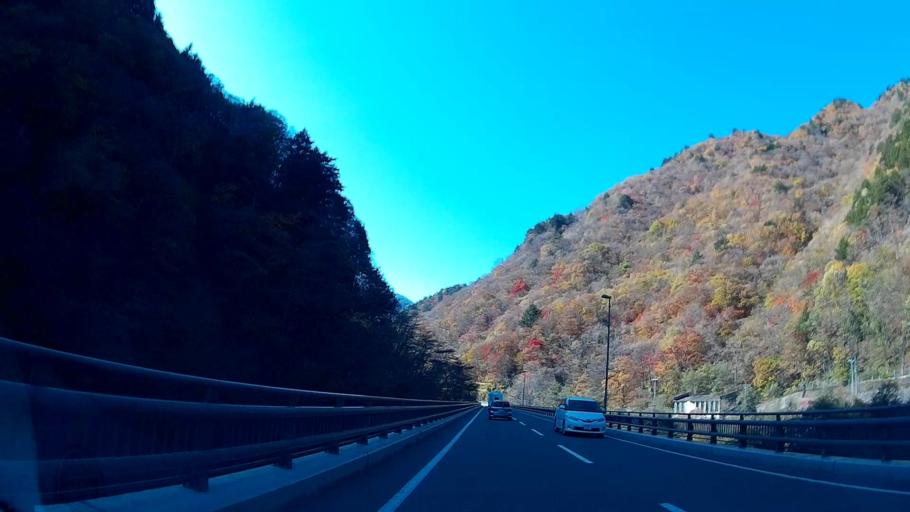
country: JP
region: Nagano
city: Toyoshina
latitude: 36.1638
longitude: 137.6672
